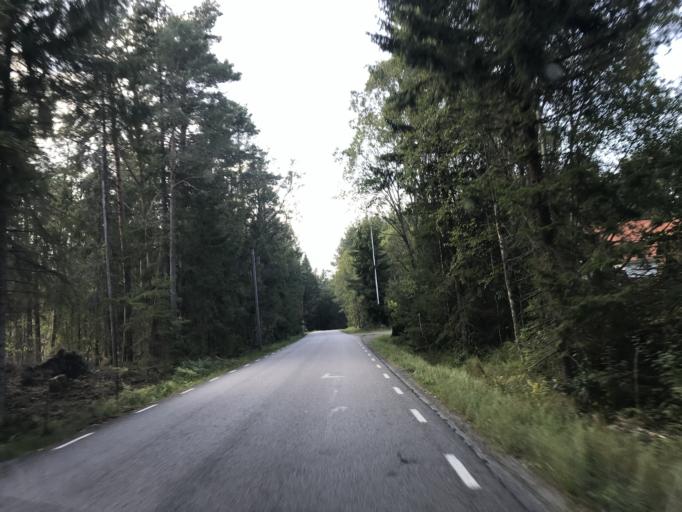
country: SE
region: Stockholm
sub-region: Norrtalje Kommun
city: Bjorko
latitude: 59.8748
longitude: 19.0117
